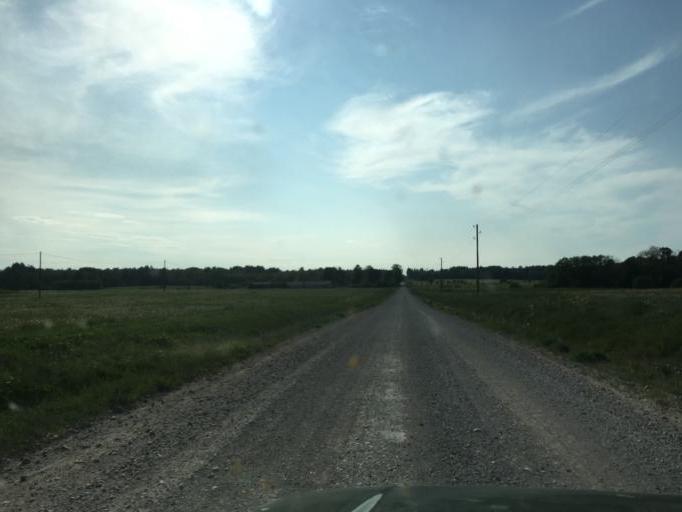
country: LV
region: Dundaga
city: Dundaga
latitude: 57.6236
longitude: 22.4005
